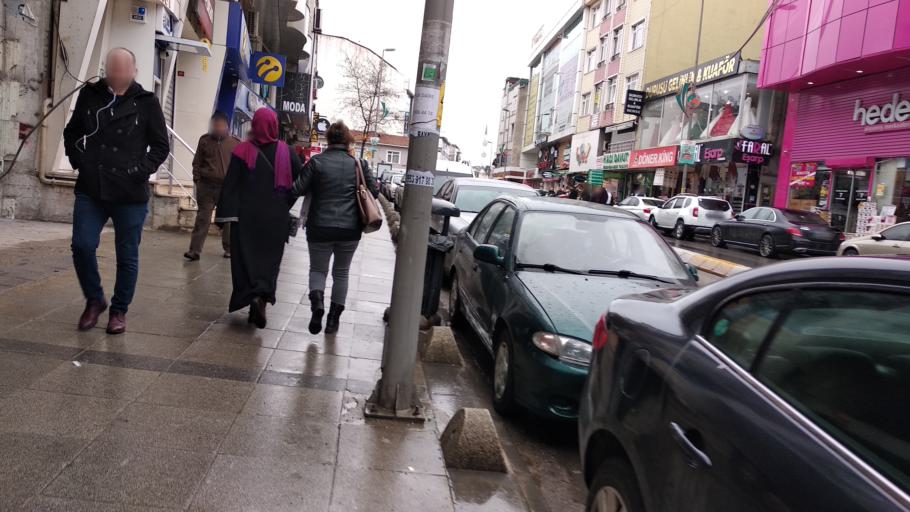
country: TR
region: Istanbul
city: Samandira
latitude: 41.0189
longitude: 29.1922
